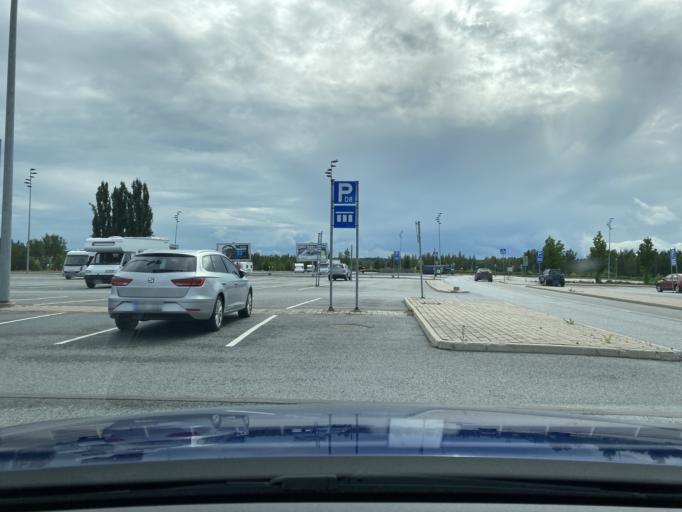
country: FI
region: Pirkanmaa
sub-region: Tampere
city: Lempaeaelae
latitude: 61.3585
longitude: 23.7960
